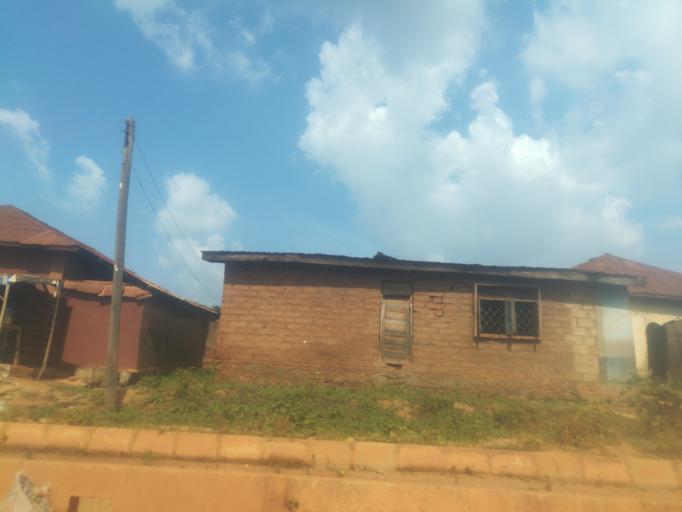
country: NG
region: Ogun
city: Abeokuta
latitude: 7.1745
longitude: 3.3555
